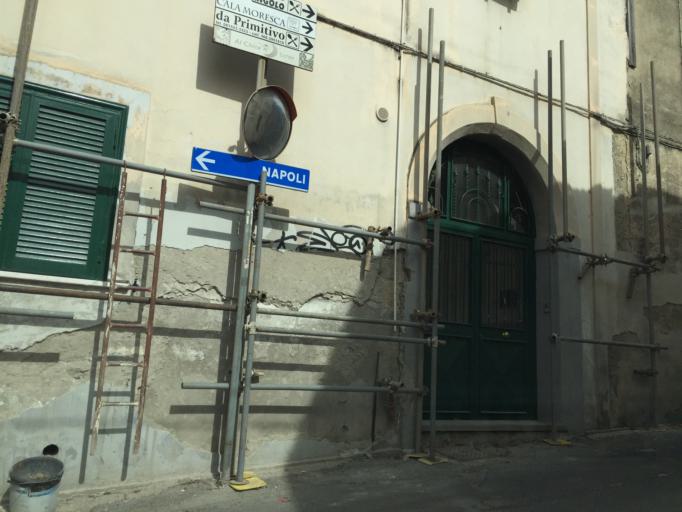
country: IT
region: Campania
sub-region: Provincia di Napoli
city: Bacoli
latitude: 40.7858
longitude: 14.0859
